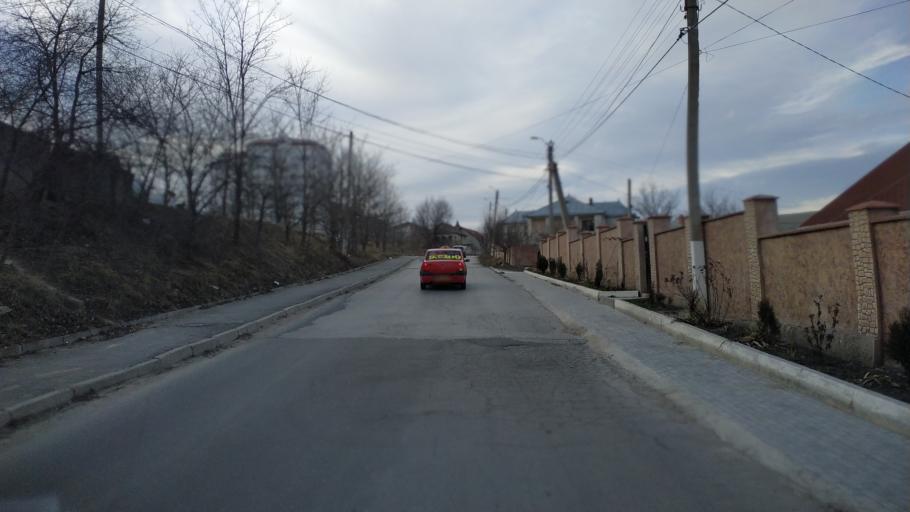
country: MD
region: Laloveni
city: Ialoveni
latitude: 46.9552
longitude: 28.7616
